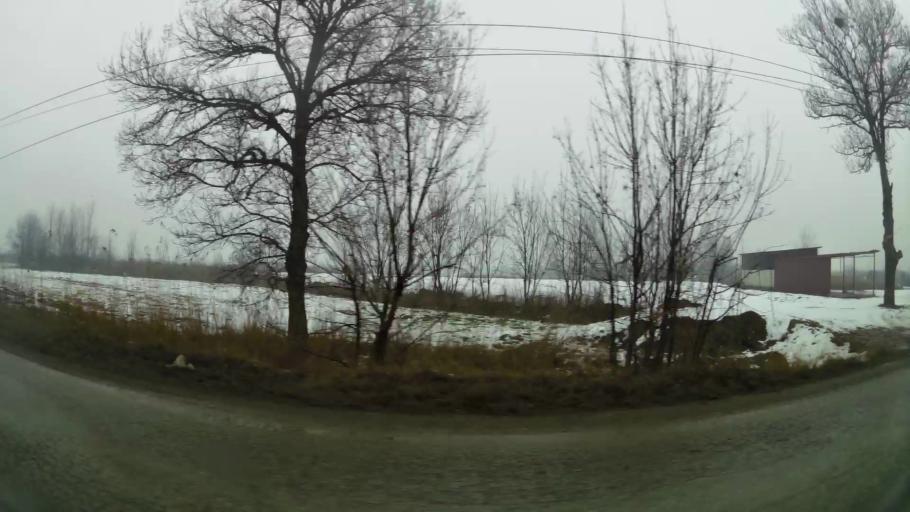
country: MK
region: Petrovec
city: Petrovec
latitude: 41.9437
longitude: 21.6032
